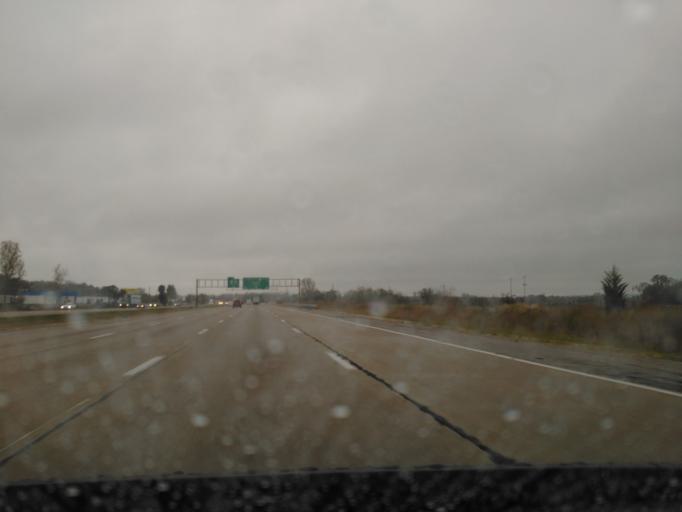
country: US
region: Illinois
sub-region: Saint Clair County
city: Dupo
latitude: 38.4853
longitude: -90.2207
